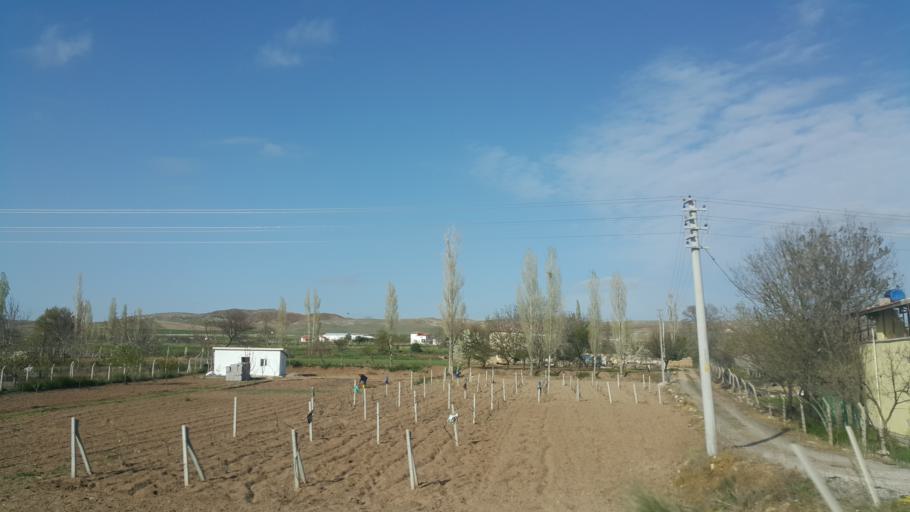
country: TR
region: Aksaray
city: Acipinar
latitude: 38.4979
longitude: 33.8710
